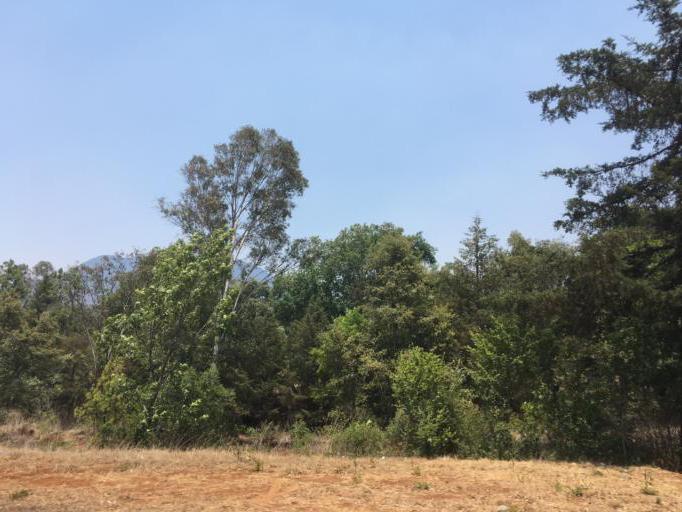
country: MX
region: Michoacan
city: Quiroga
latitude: 19.6537
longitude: -101.4951
